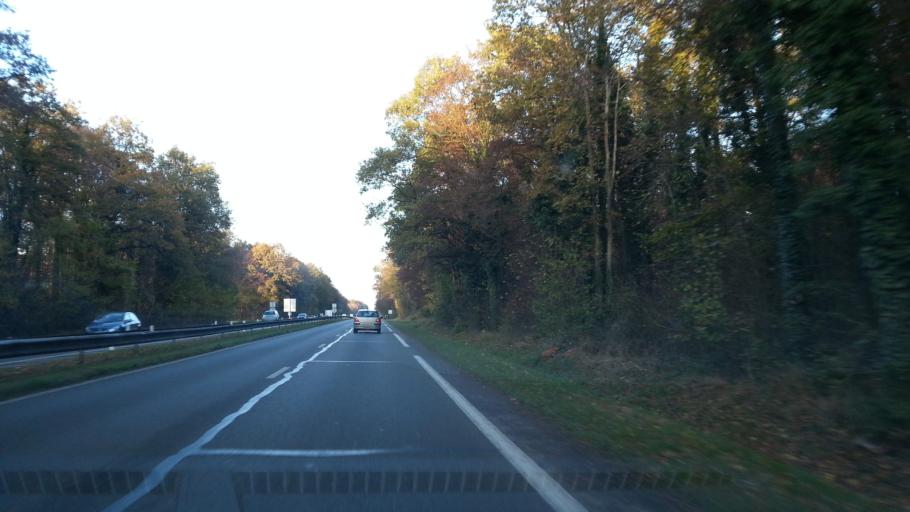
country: FR
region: Picardie
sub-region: Departement de l'Oise
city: Saint-Maximin
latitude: 49.2089
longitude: 2.4632
